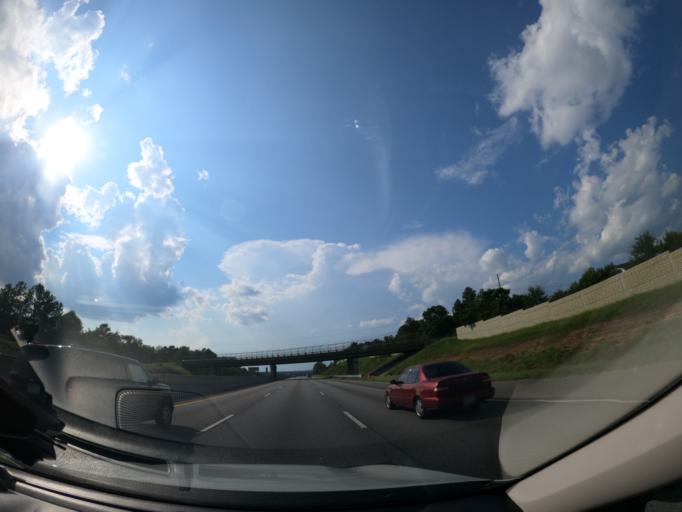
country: US
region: Georgia
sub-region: Columbia County
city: Martinez
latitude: 33.4283
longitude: -82.0640
